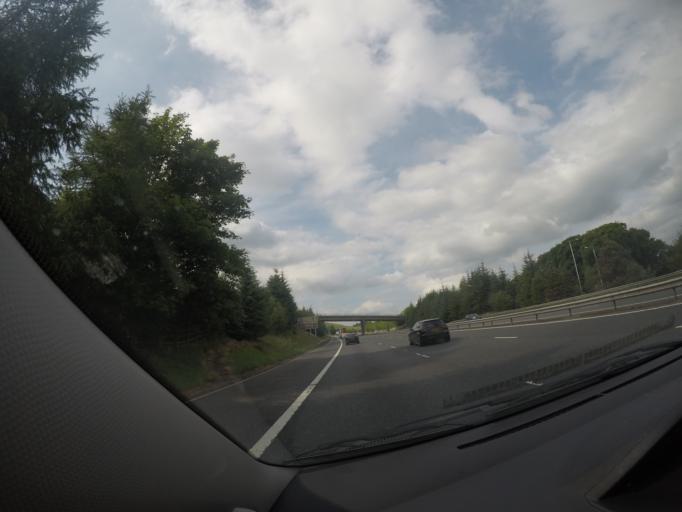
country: GB
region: Scotland
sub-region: South Lanarkshire
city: Douglas
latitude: 55.4885
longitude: -3.6956
